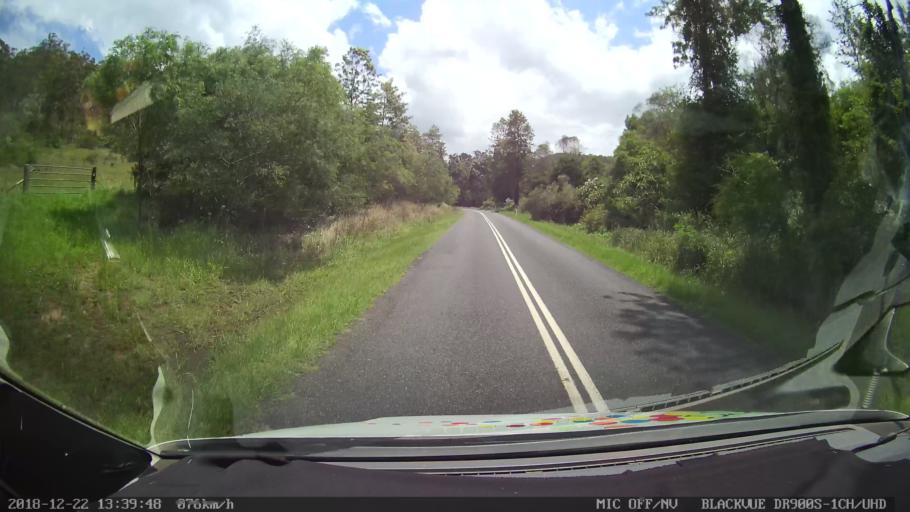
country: AU
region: New South Wales
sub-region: Clarence Valley
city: Coutts Crossing
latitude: -29.9140
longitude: 152.7834
